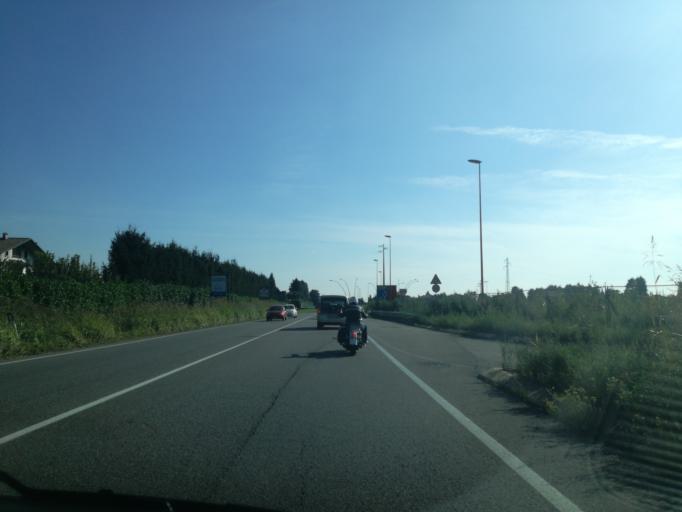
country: IT
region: Lombardy
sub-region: Provincia di Bergamo
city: Ambivere
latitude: 45.7211
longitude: 9.5555
